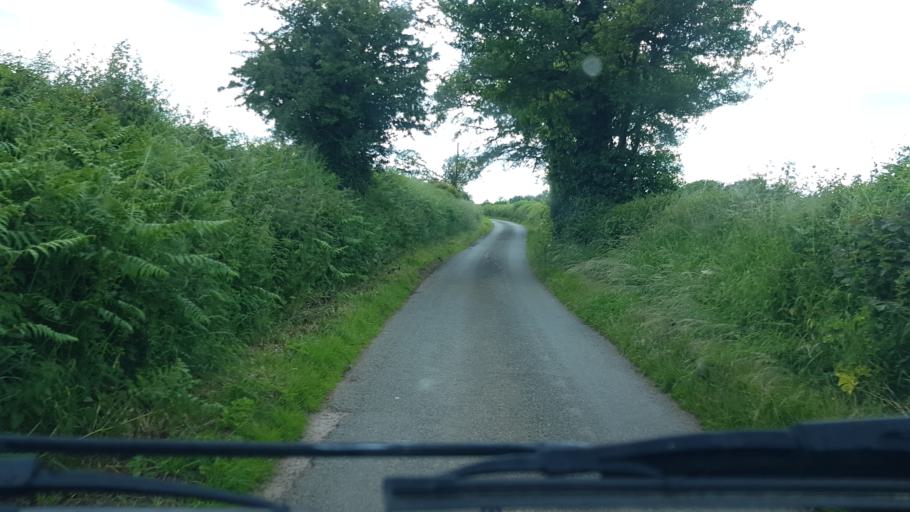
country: GB
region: England
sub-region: Shropshire
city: Romsley
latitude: 52.4508
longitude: -2.3027
